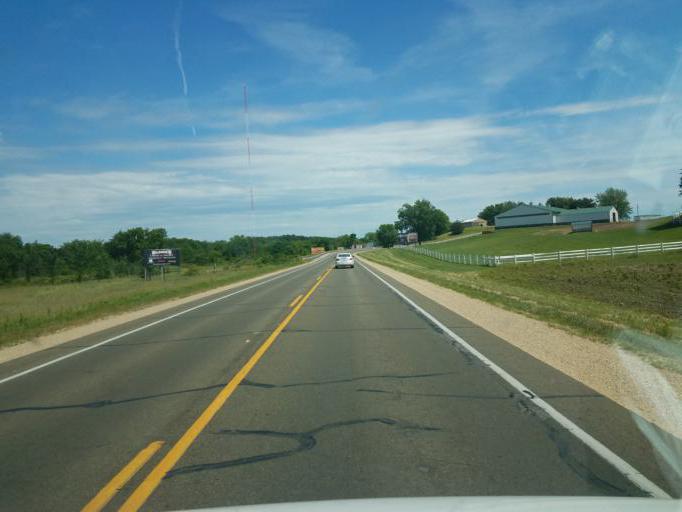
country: US
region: Wisconsin
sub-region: Sauk County
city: Reedsburg
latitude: 43.5419
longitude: -90.0392
